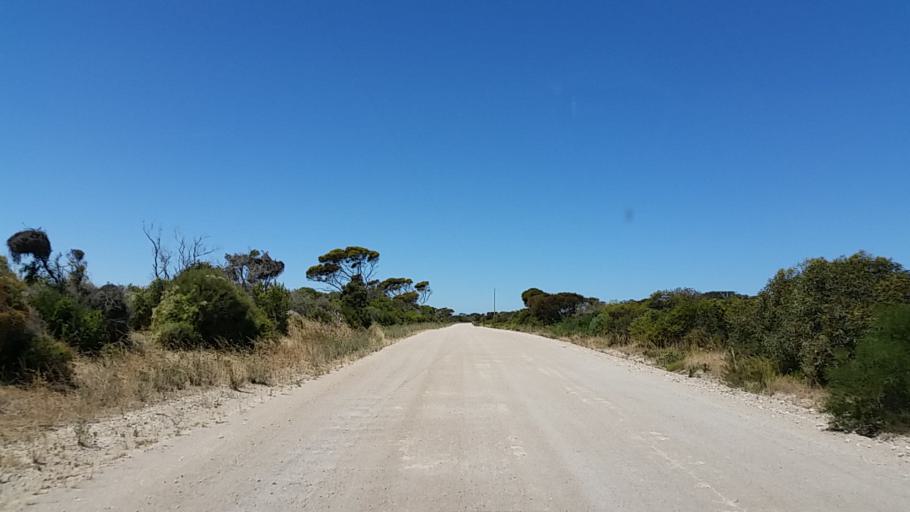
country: AU
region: South Australia
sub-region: Yorke Peninsula
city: Honiton
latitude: -35.1187
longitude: 137.3583
